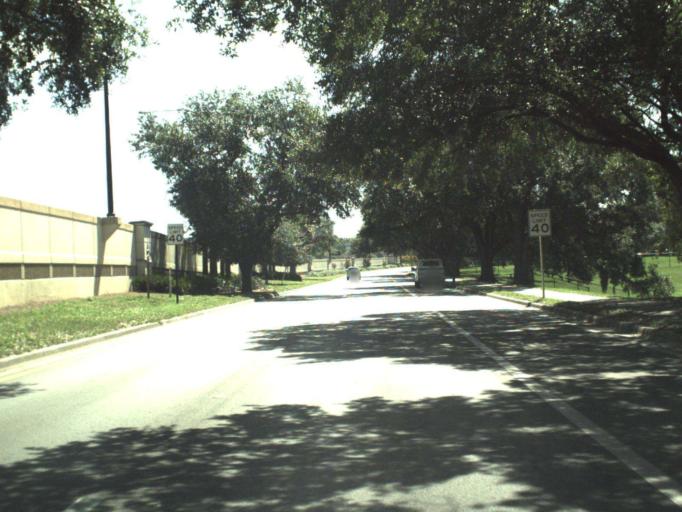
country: US
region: Florida
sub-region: Orange County
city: Orlando
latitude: 28.5372
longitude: -81.3621
